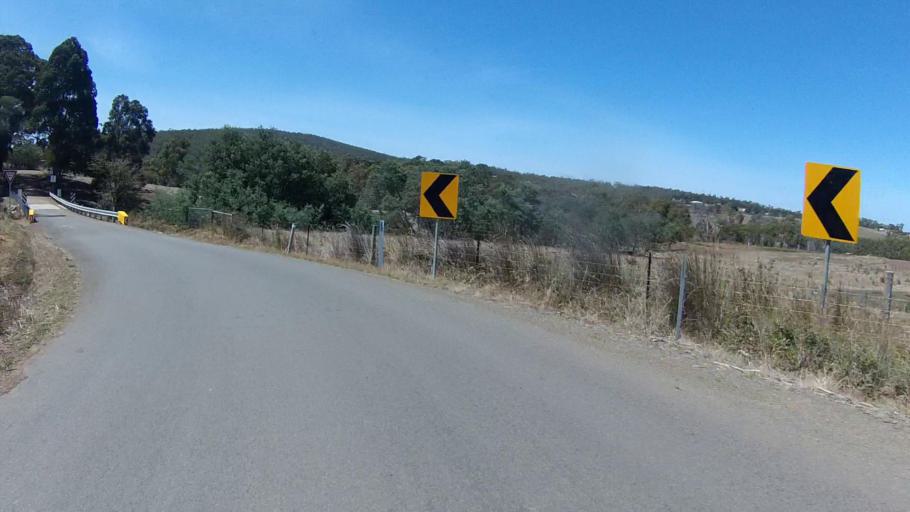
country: AU
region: Tasmania
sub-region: Sorell
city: Sorell
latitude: -42.7982
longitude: 147.6404
